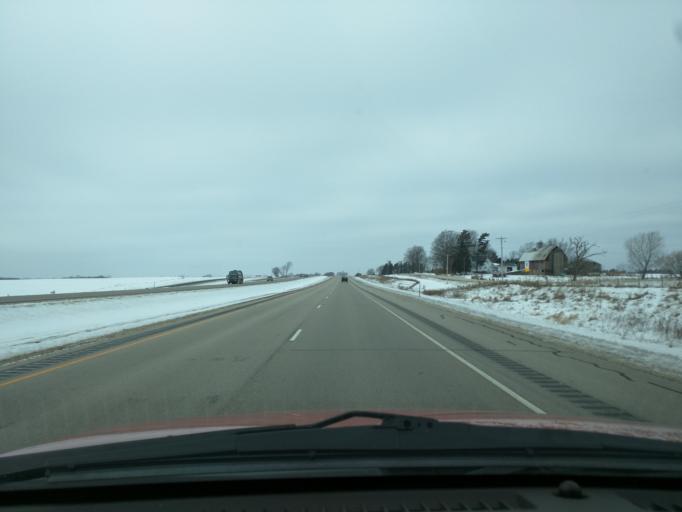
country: US
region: Wisconsin
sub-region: Trempealeau County
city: Trempealeau
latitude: 43.9244
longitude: -91.4644
